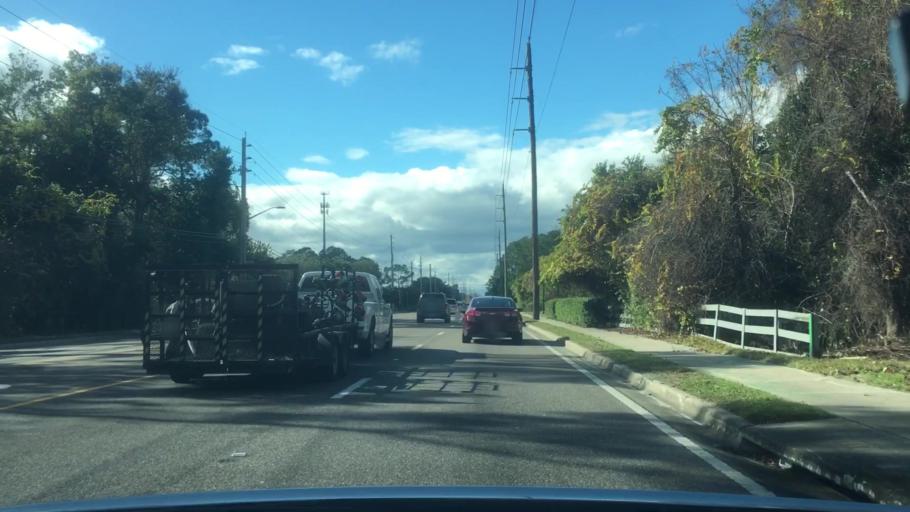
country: US
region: Florida
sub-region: Duval County
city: Jacksonville
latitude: 30.3524
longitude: -81.5630
